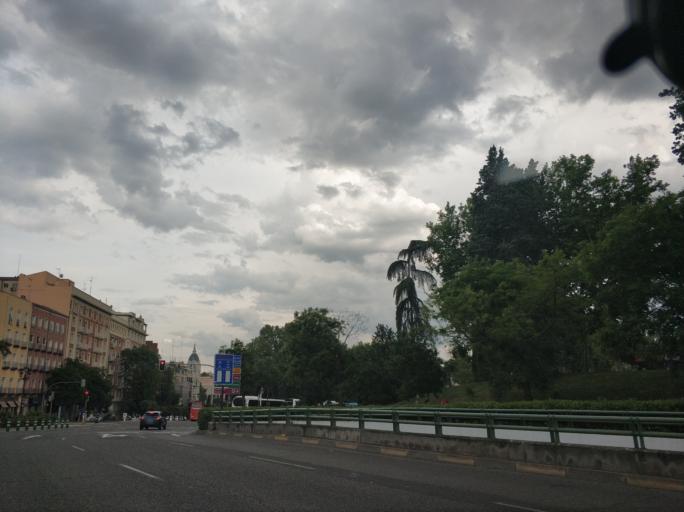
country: ES
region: Madrid
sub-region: Provincia de Madrid
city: City Center
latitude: 40.4252
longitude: -3.7167
